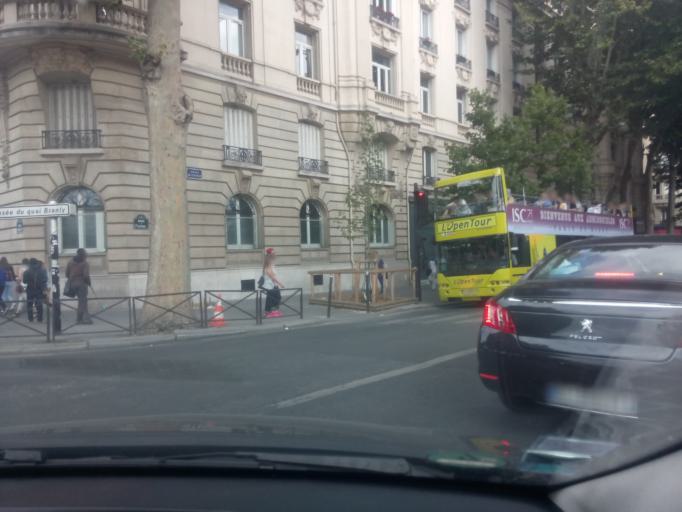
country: FR
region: Ile-de-France
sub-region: Departement des Hauts-de-Seine
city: Vanves
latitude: 48.8575
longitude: 2.2910
